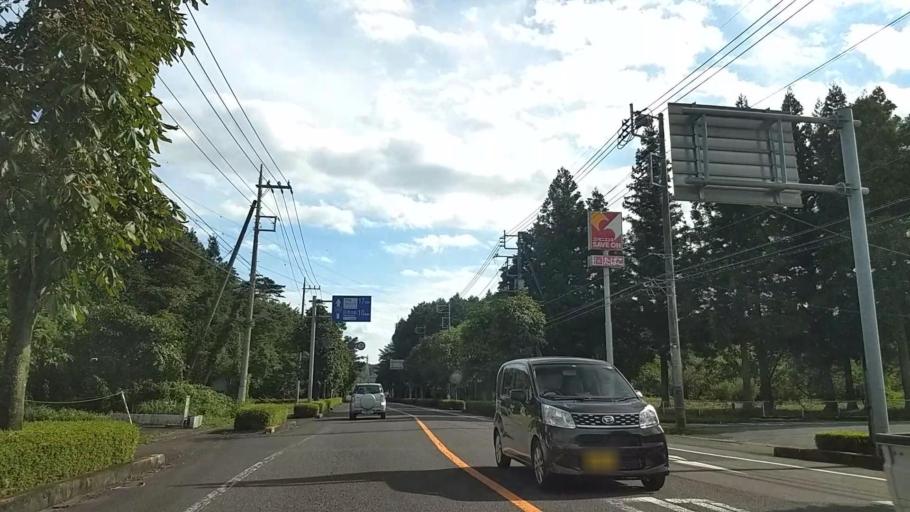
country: JP
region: Tochigi
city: Imaichi
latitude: 36.7941
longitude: 139.7014
